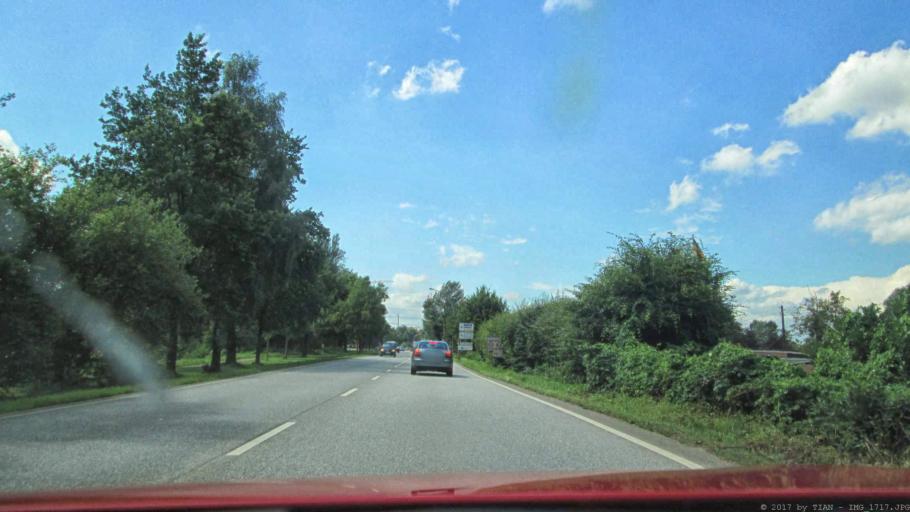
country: DE
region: Hamburg
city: Harburg
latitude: 53.4634
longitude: 10.0142
